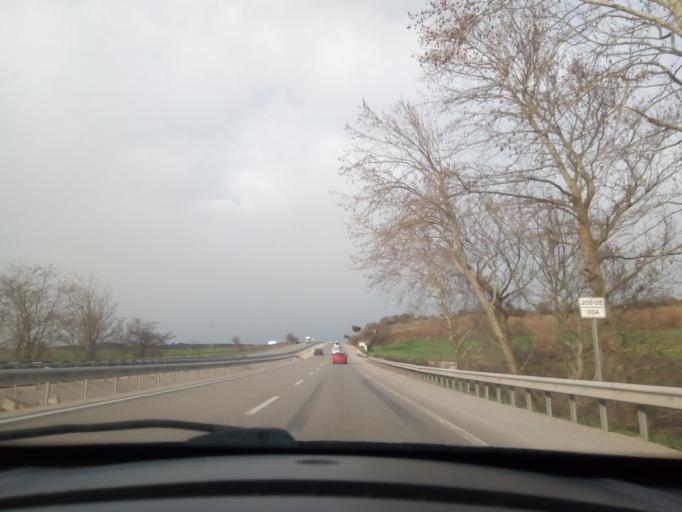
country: TR
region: Bursa
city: Mahmudiye
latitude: 40.2143
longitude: 28.6700
